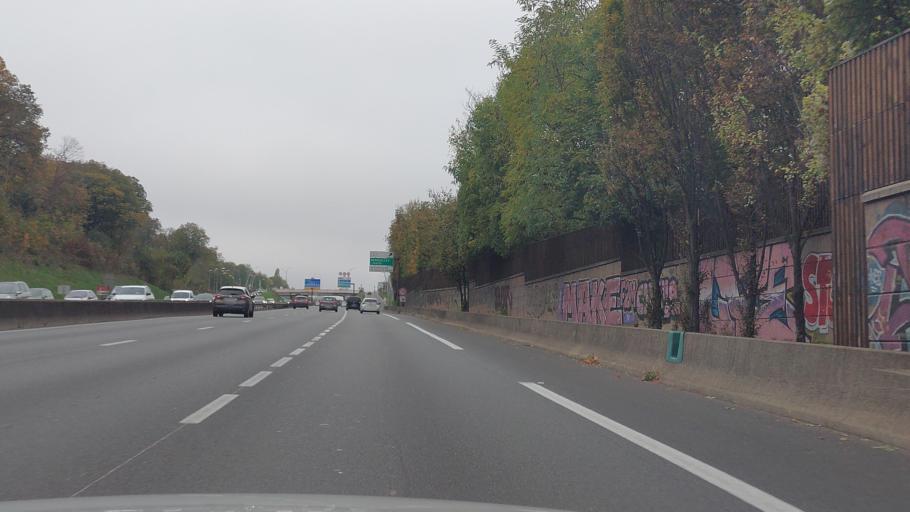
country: FR
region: Ile-de-France
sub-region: Departement des Hauts-de-Seine
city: Vaucresson
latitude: 48.8326
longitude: 2.1599
